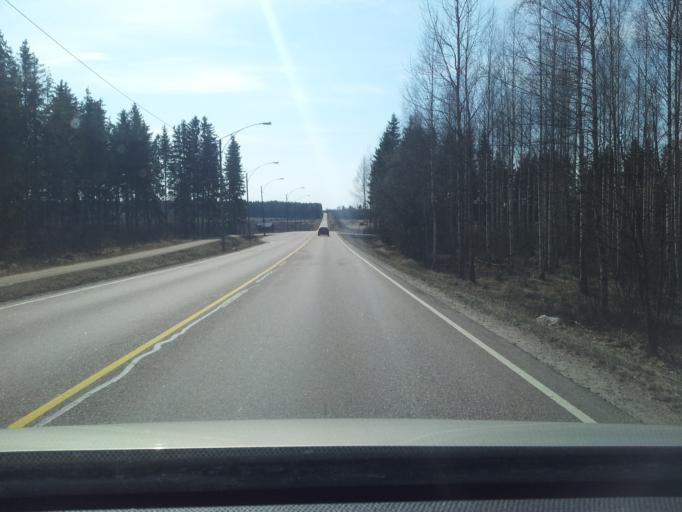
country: FI
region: Kymenlaakso
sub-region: Kotka-Hamina
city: Hamina
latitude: 60.6275
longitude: 27.2095
